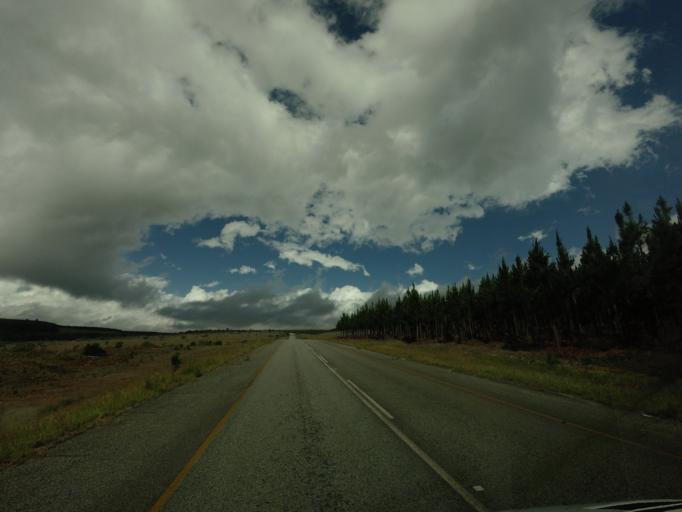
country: ZA
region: Mpumalanga
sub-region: Ehlanzeni District
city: Graksop
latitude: -24.8643
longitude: 30.8550
